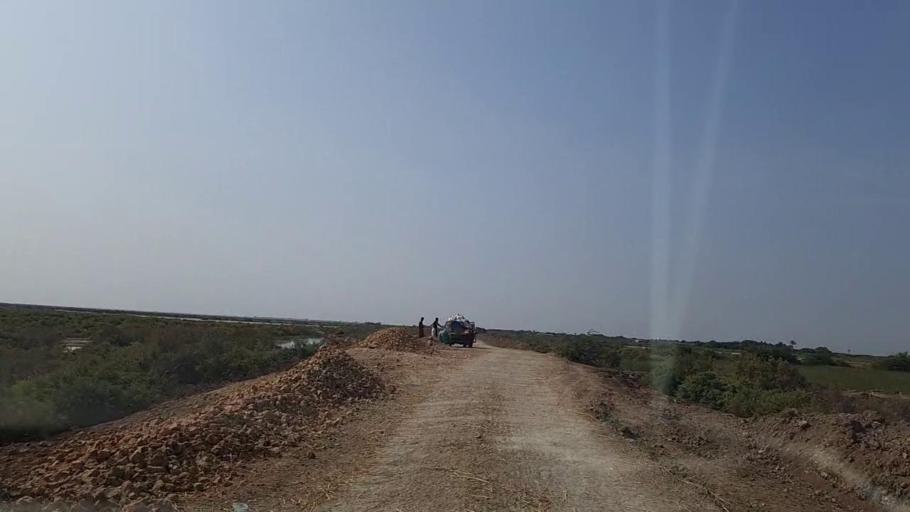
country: PK
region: Sindh
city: Chuhar Jamali
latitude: 24.1992
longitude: 67.8304
